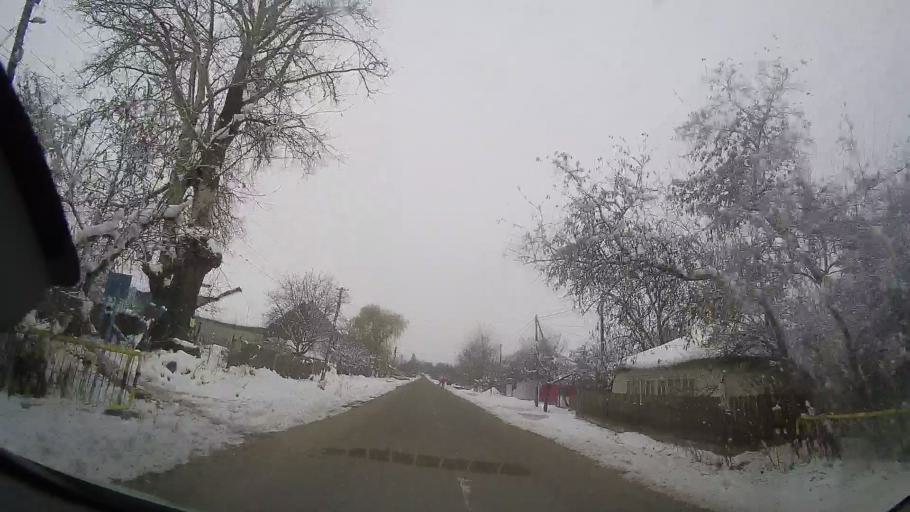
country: RO
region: Vaslui
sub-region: Comuna Bacesti
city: Bacesti
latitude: 46.8162
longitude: 27.2046
